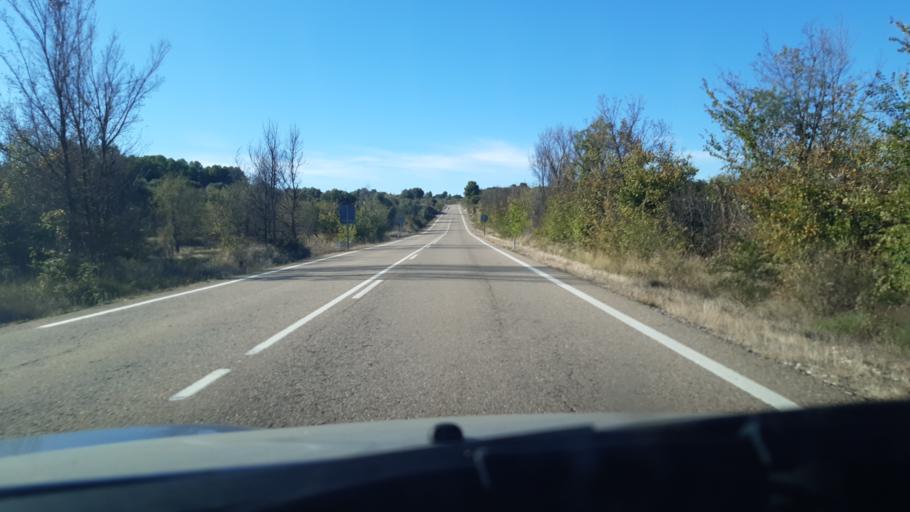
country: ES
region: Aragon
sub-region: Provincia de Teruel
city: Valjunquera
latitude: 40.9603
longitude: -0.0069
